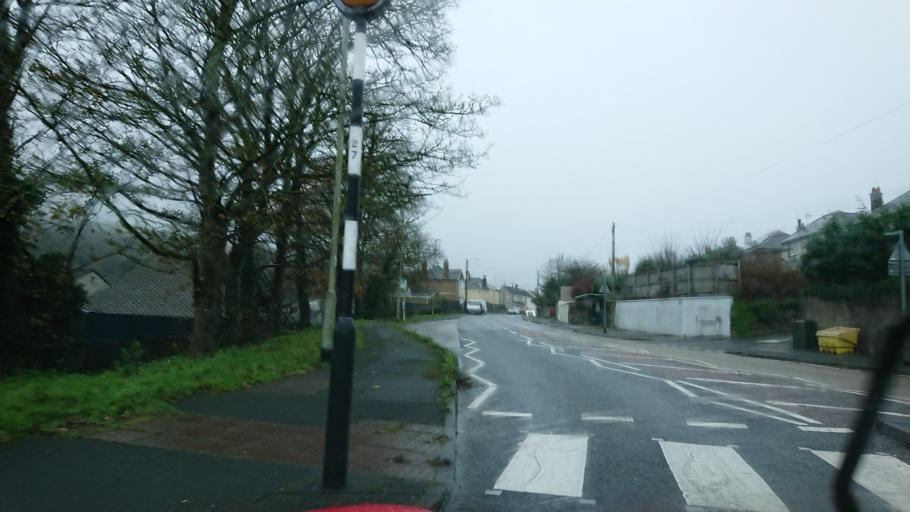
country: GB
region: England
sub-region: Plymouth
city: Plymstock
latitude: 50.3521
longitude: -4.1037
